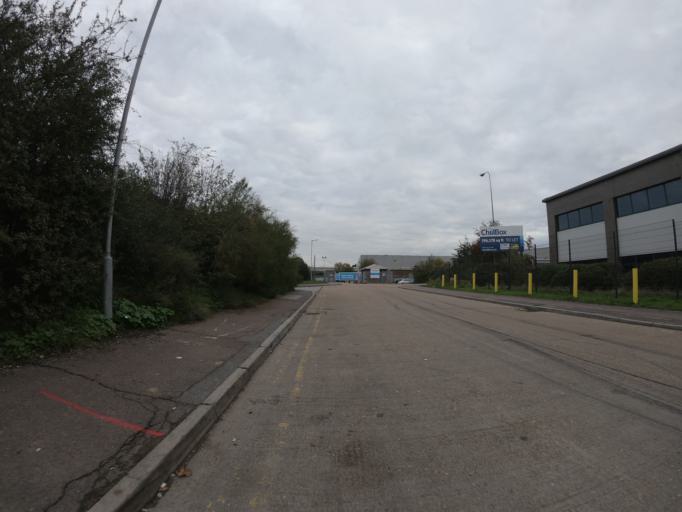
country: GB
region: England
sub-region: Kent
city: West Thurrock
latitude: 51.4792
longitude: 0.2699
